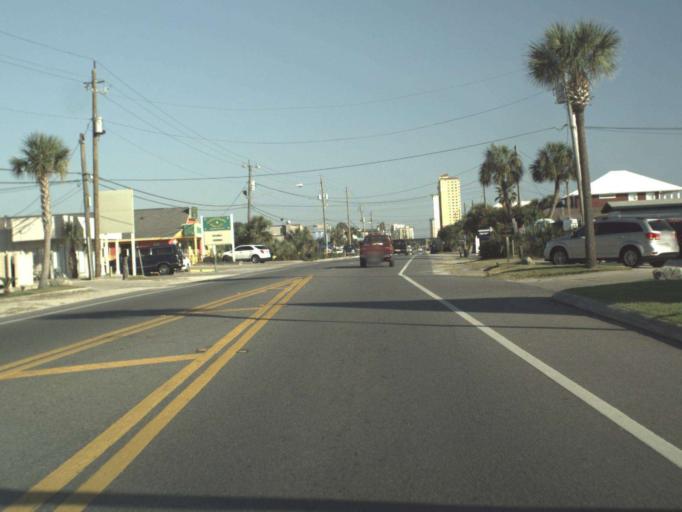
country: US
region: Florida
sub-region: Bay County
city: Laguna Beach
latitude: 30.2193
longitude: -85.8835
